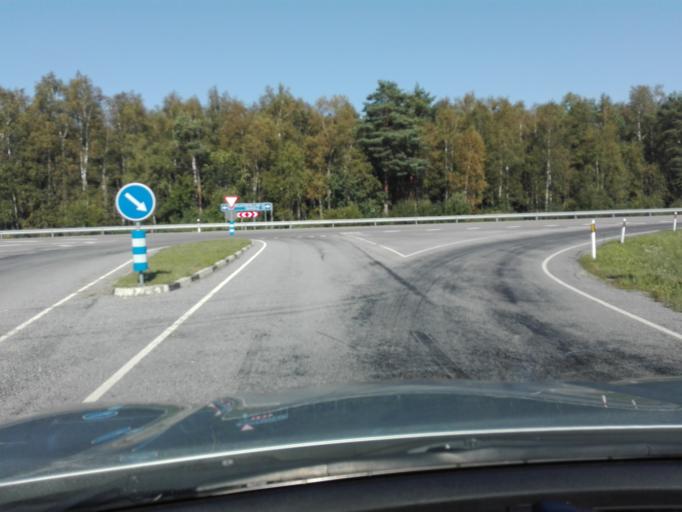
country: EE
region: Raplamaa
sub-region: Rapla vald
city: Rapla
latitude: 59.0191
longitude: 24.7822
